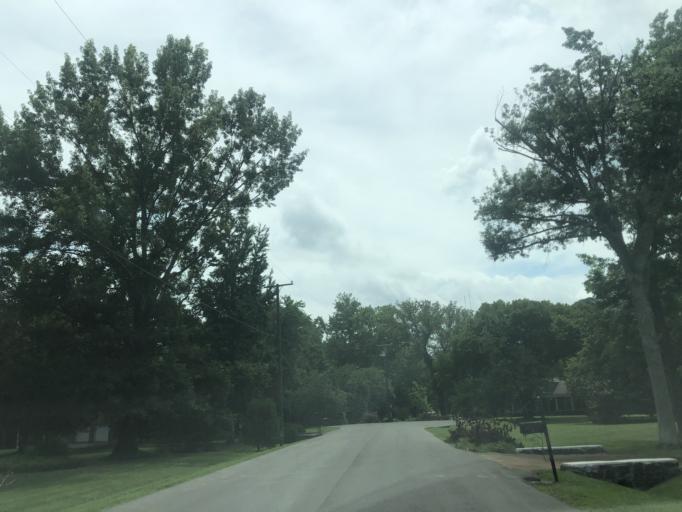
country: US
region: Tennessee
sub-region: Davidson County
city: Forest Hills
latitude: 36.0632
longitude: -86.8163
